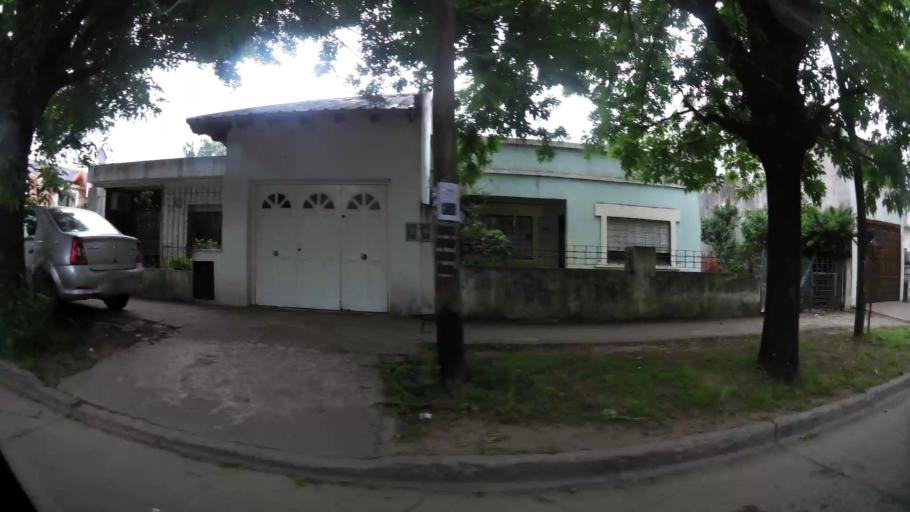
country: AR
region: Buenos Aires
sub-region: Partido de Ezeiza
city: Ezeiza
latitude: -34.8598
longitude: -58.5188
